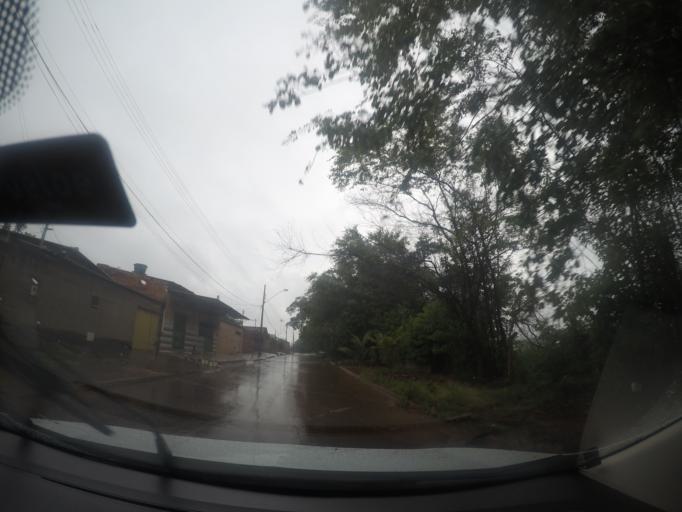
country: BR
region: Goias
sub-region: Goianira
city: Goianira
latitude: -16.5925
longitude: -49.3545
